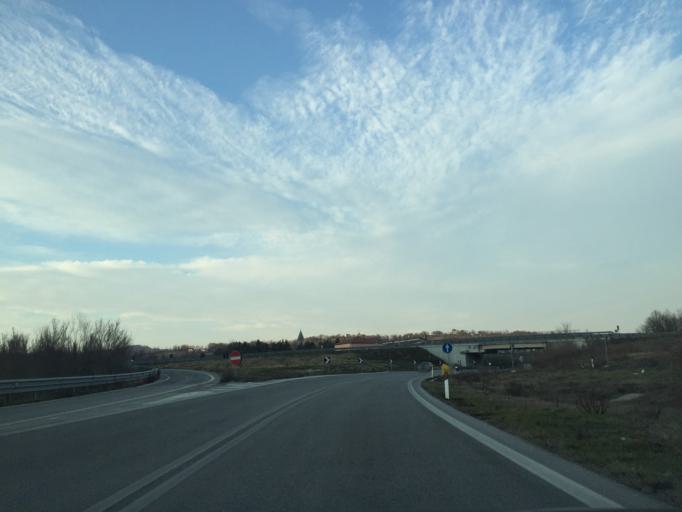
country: IT
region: Molise
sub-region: Provincia di Campobasso
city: Vinchiaturo
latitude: 41.4732
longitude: 14.5593
